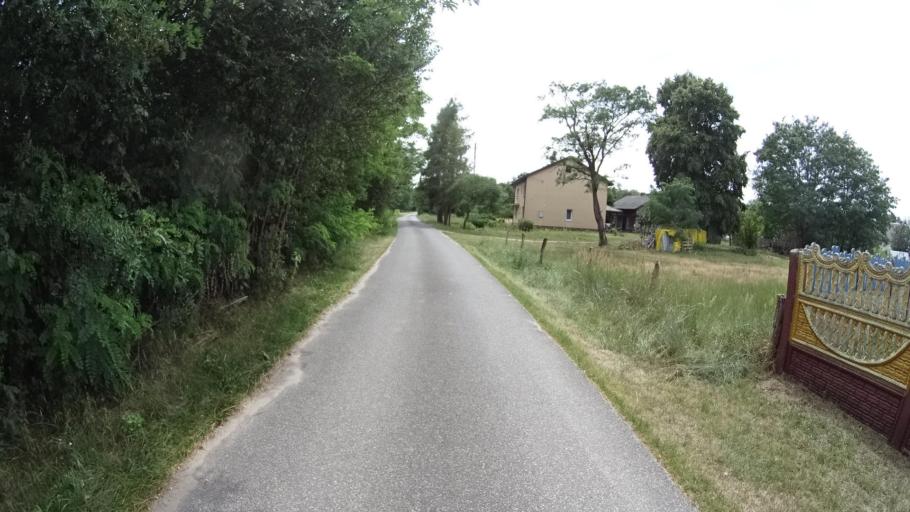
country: PL
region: Masovian Voivodeship
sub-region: Powiat bialobrzeski
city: Bialobrzegi
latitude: 51.6452
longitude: 20.9036
